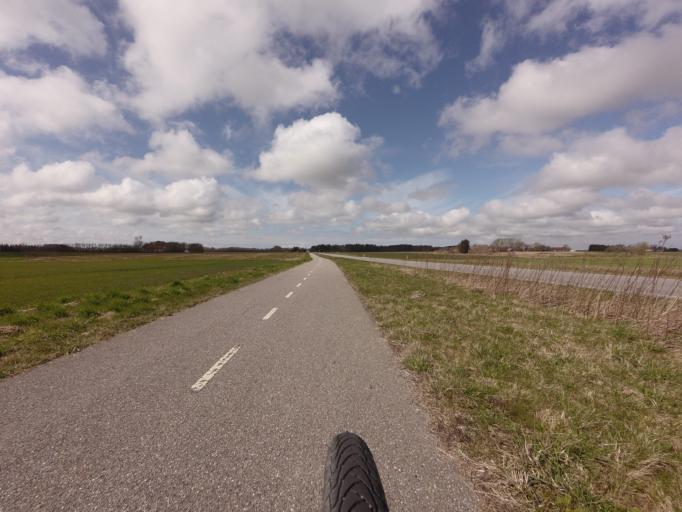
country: DK
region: North Denmark
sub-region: Hjorring Kommune
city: Vra
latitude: 57.3541
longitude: 9.8959
